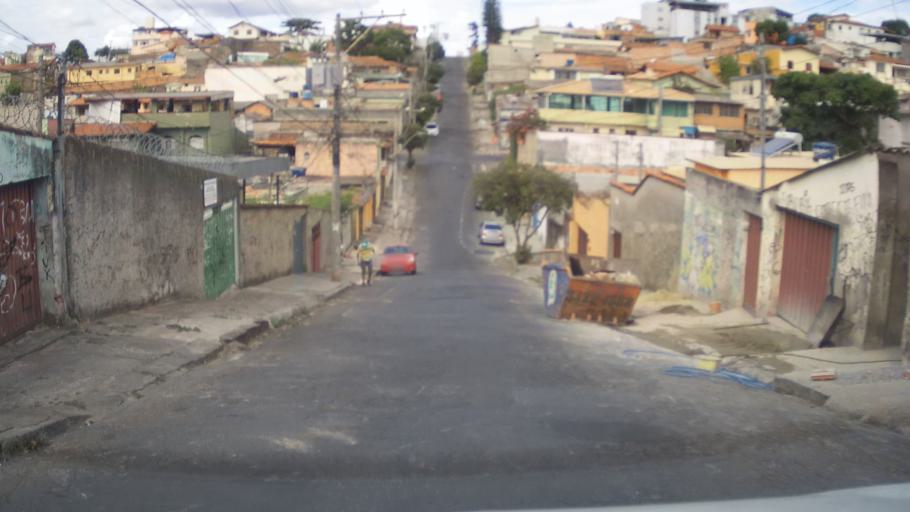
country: BR
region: Minas Gerais
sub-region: Belo Horizonte
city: Belo Horizonte
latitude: -19.9011
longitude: -43.9384
